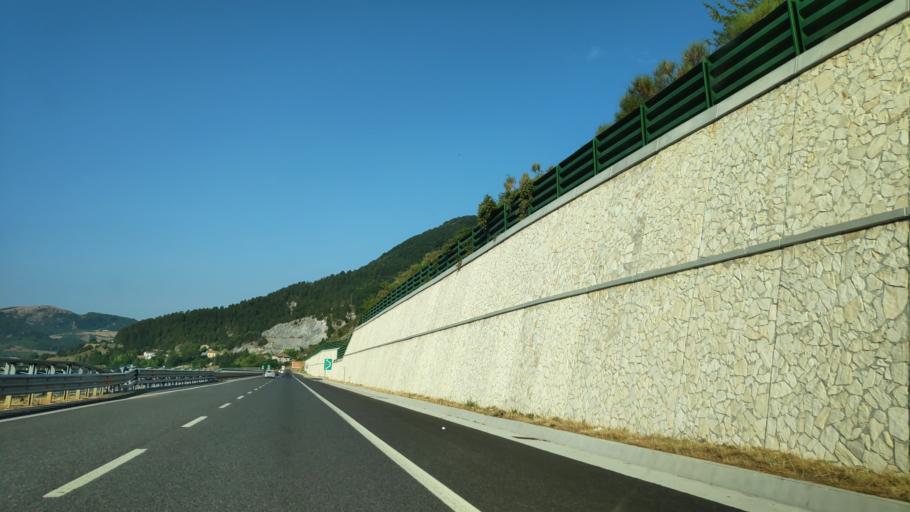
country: IT
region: Calabria
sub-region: Provincia di Cosenza
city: Mormanno
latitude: 39.8848
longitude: 16.0184
